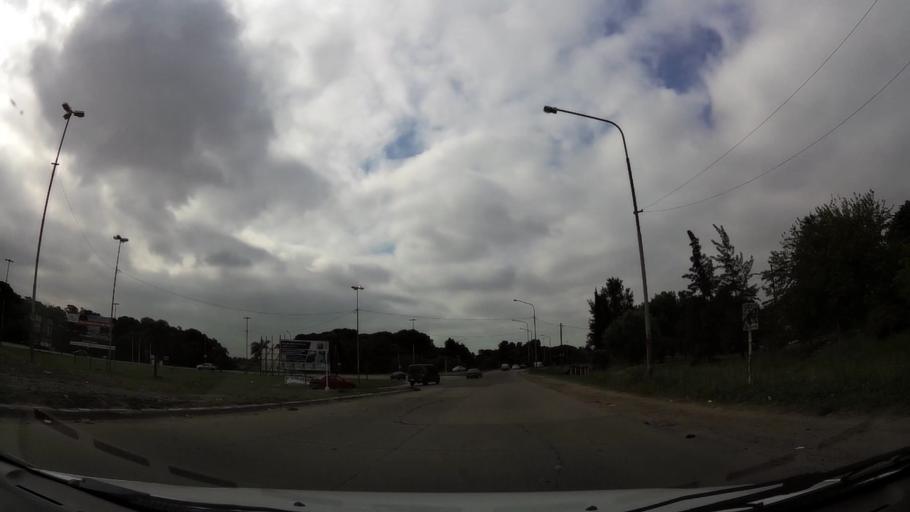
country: AR
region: Buenos Aires
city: San Justo
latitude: -34.7228
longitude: -58.5349
